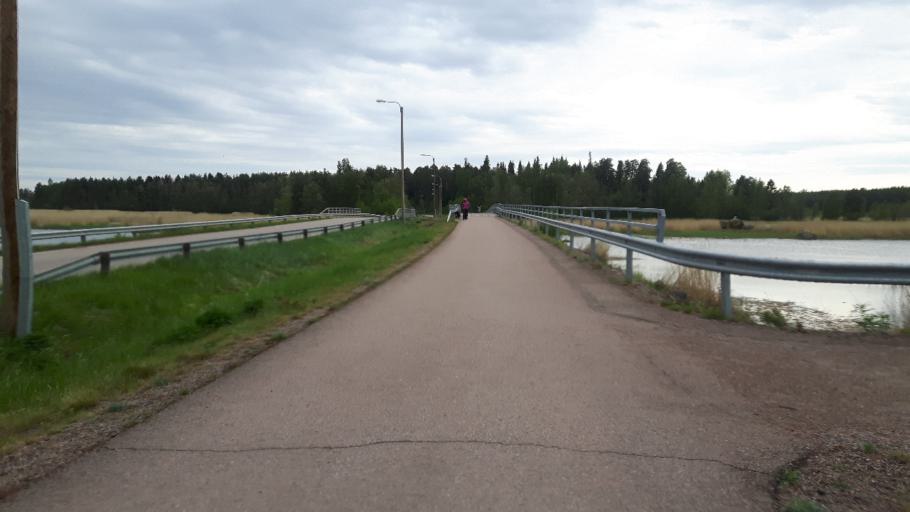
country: FI
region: Kymenlaakso
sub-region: Kotka-Hamina
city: Hamina
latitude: 60.5508
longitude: 27.2288
